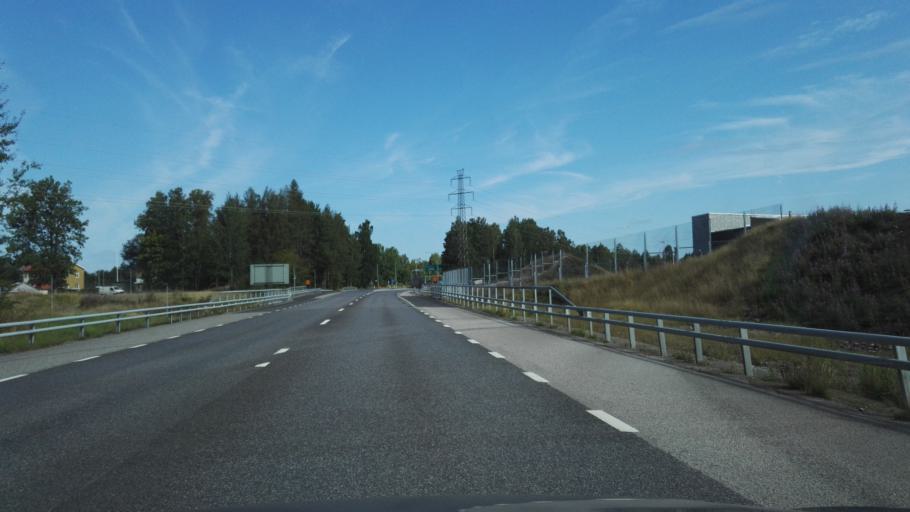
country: SE
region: Kronoberg
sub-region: Vaxjo Kommun
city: Vaexjoe
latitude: 56.8757
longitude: 14.7426
